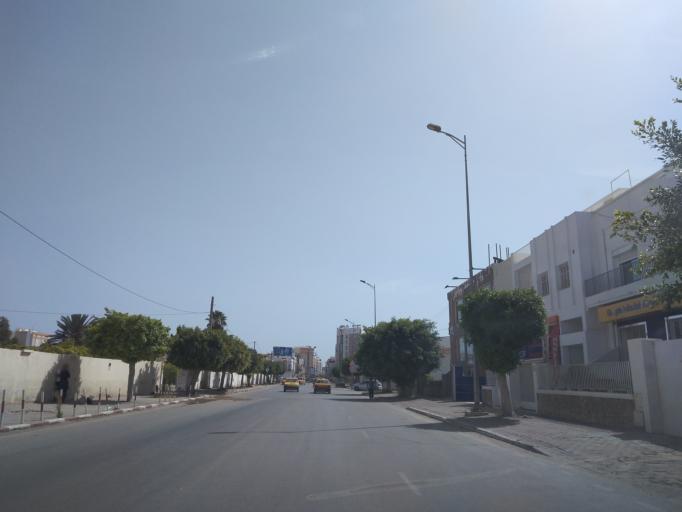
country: TN
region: Safaqis
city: Sfax
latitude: 34.7325
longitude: 10.7496
